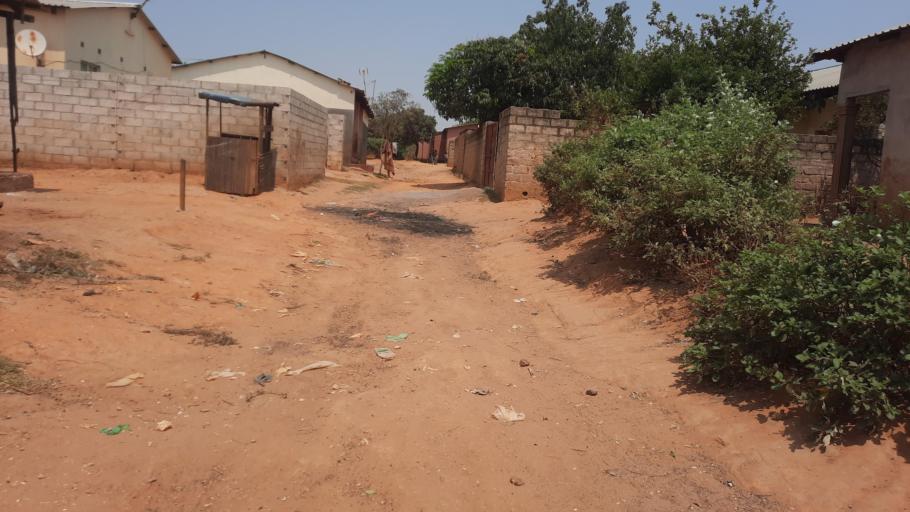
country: ZM
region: Lusaka
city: Lusaka
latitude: -15.3981
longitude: 28.3803
